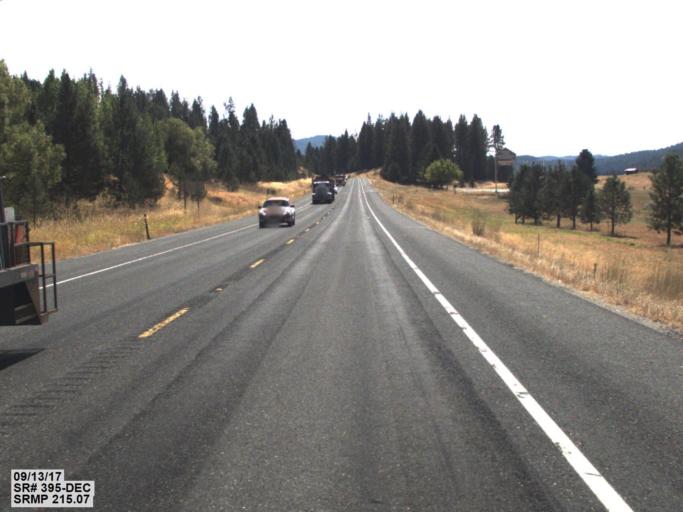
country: US
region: Washington
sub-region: Stevens County
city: Chewelah
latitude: 48.3464
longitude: -117.8330
